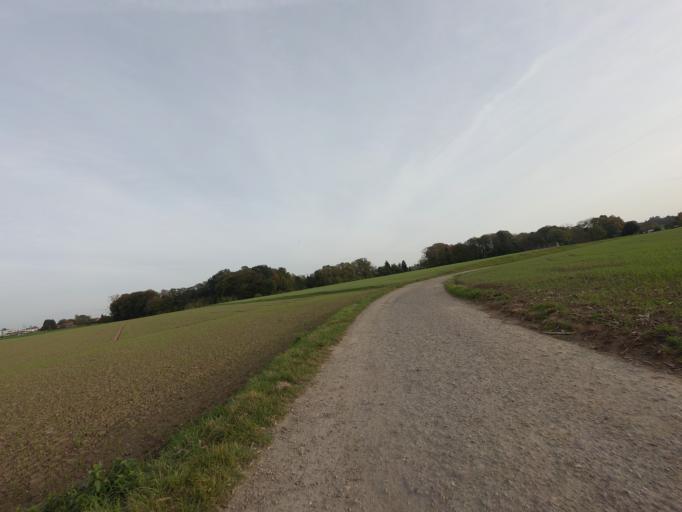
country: BE
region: Flanders
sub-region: Provincie Vlaams-Brabant
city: Herent
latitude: 50.9067
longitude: 4.6564
